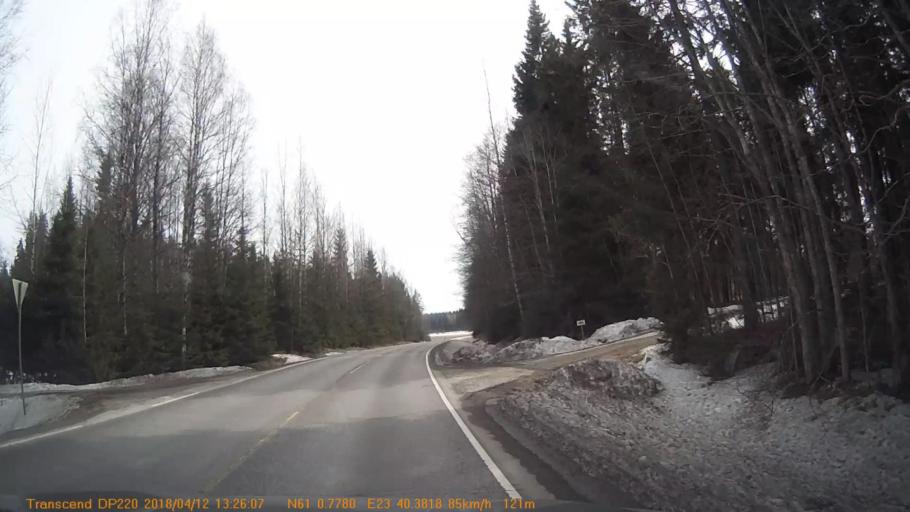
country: FI
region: Pirkanmaa
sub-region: Etelae-Pirkanmaa
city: Kylmaekoski
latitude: 61.0128
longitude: 23.6732
